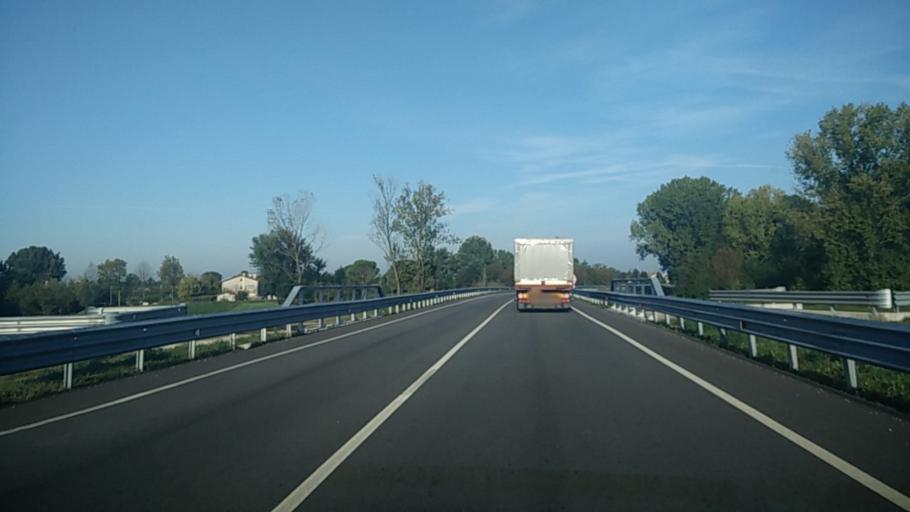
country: IT
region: Veneto
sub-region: Provincia di Venezia
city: Martellago
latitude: 45.5525
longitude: 12.1659
